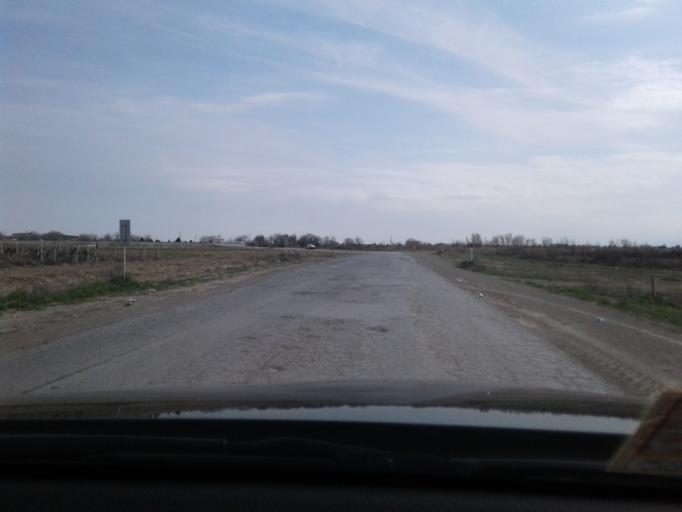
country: TM
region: Ahal
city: Ashgabat
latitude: 38.1161
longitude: 58.3607
